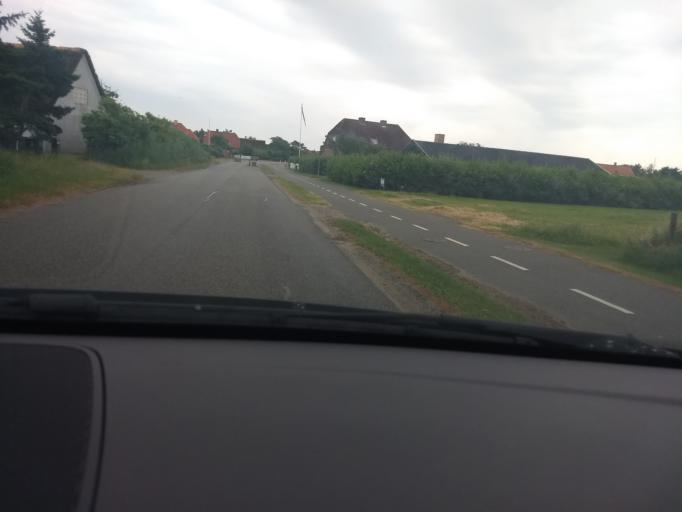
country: DK
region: South Denmark
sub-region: Fano Kommune
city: Nordby
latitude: 55.3524
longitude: 8.4668
